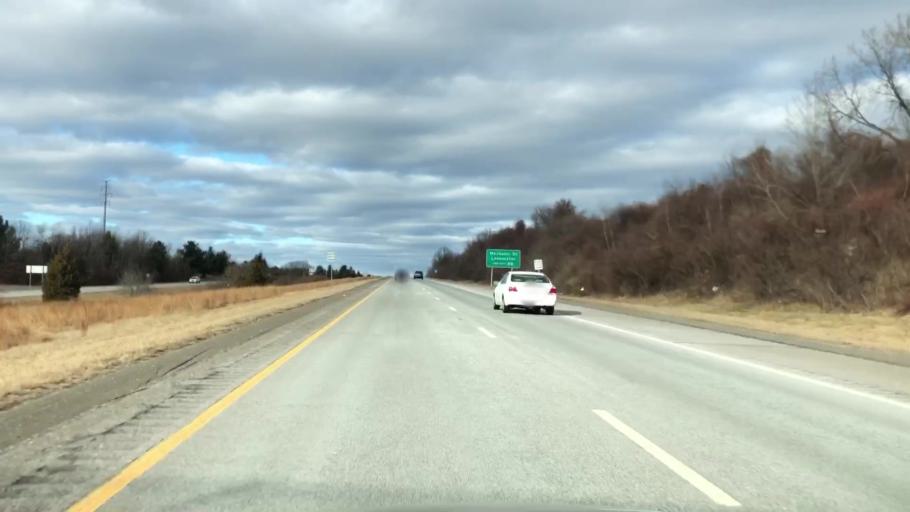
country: US
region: Massachusetts
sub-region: Worcester County
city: Leominster
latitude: 42.5082
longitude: -71.7211
